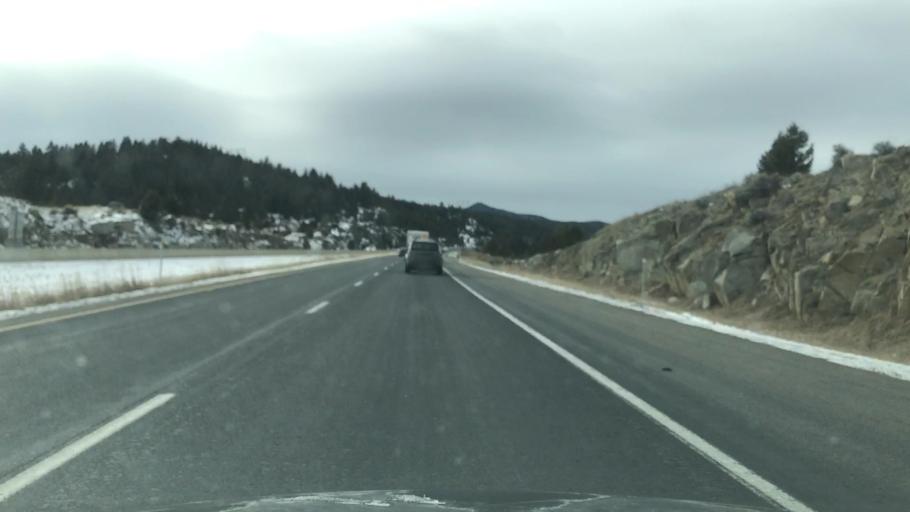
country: US
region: Montana
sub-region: Jefferson County
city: Whitehall
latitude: 45.9147
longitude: -112.2889
